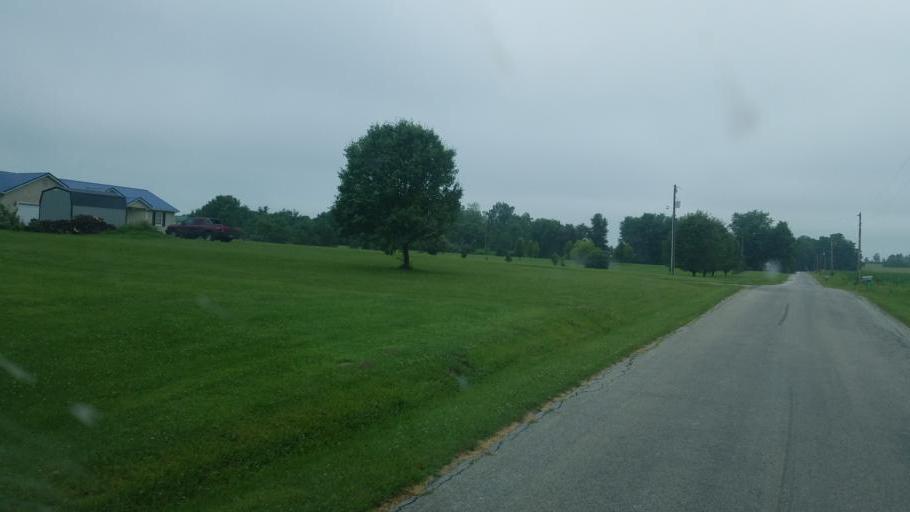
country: US
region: Ohio
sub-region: Highland County
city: Hillsboro
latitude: 39.2462
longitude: -83.5400
